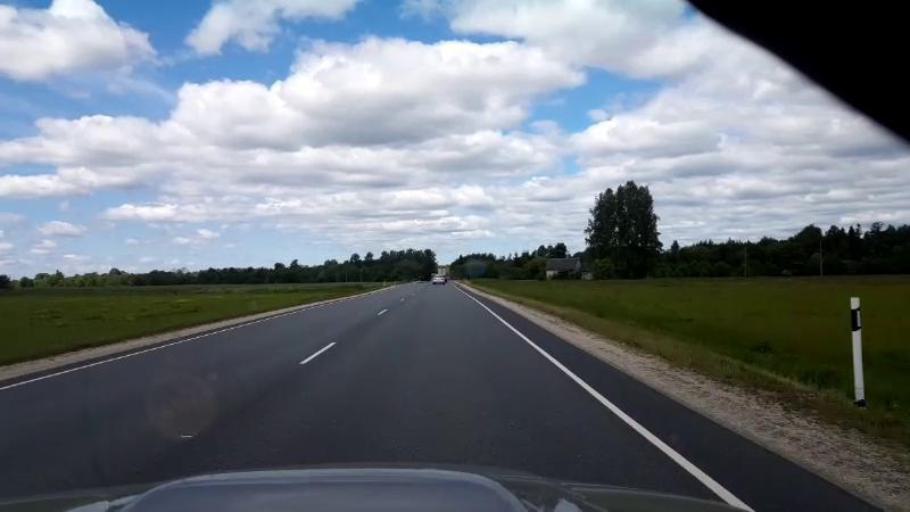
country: EE
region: Paernumaa
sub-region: Halinga vald
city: Parnu-Jaagupi
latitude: 58.6961
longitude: 24.4309
